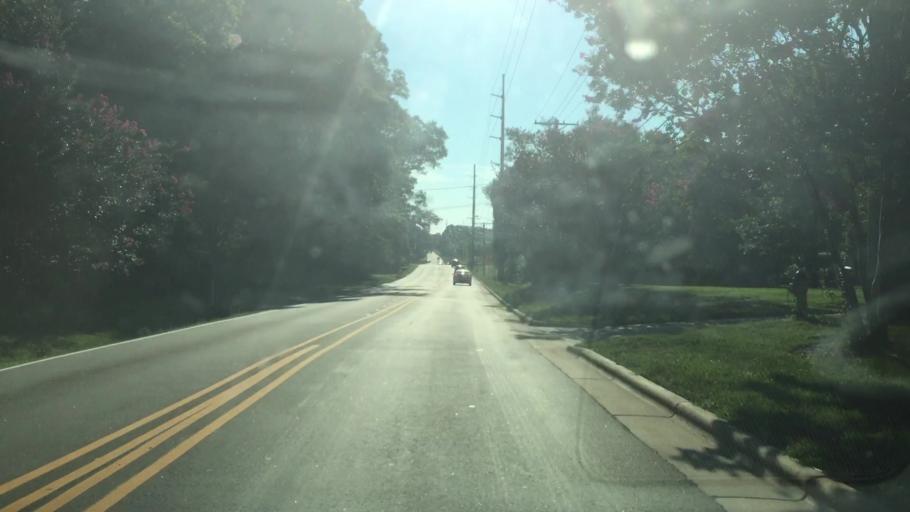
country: US
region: North Carolina
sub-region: Cabarrus County
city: Concord
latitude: 35.4145
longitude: -80.6509
